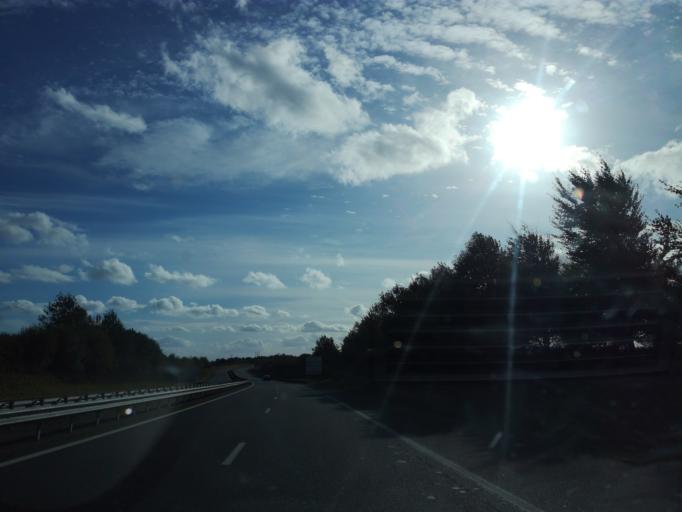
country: FR
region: Brittany
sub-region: Departement du Morbihan
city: Noyal-Pontivy
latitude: 48.0906
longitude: -2.9228
